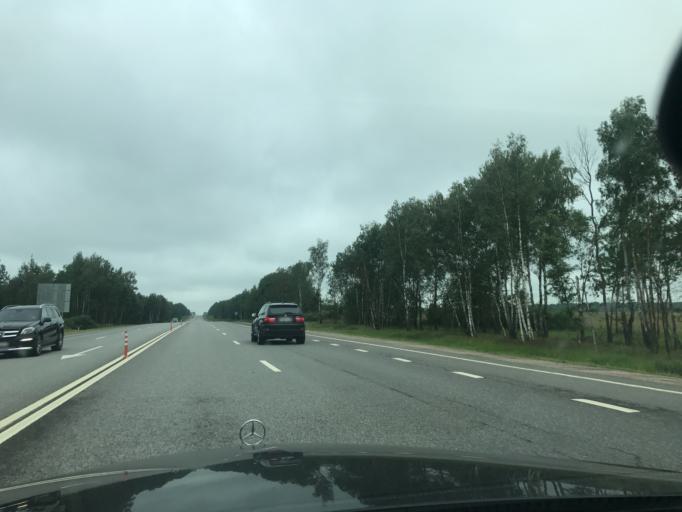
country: RU
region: Smolensk
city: Katyn'
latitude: 54.8505
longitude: 31.8344
